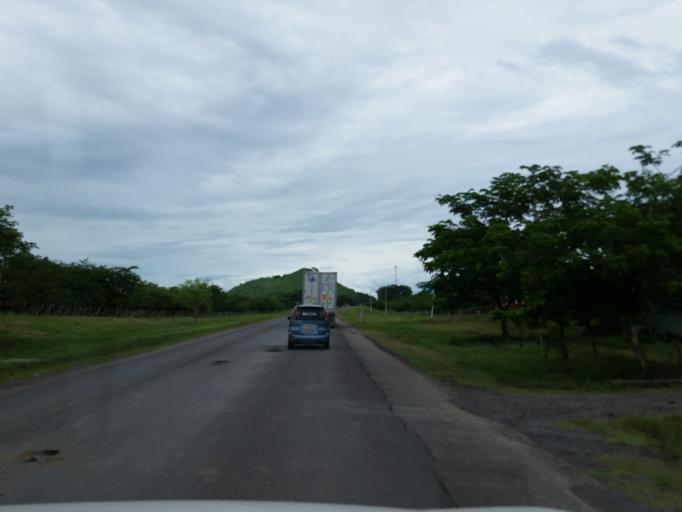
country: NI
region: Chinandega
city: Somotillo
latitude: 12.8976
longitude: -86.8511
